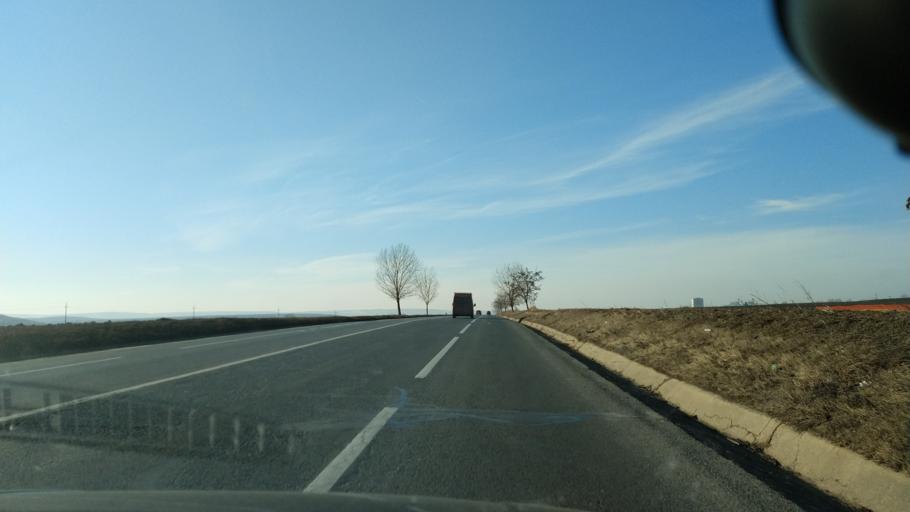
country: RO
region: Iasi
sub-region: Comuna Ion Neculce
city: Razboieni
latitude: 47.2212
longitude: 27.0790
